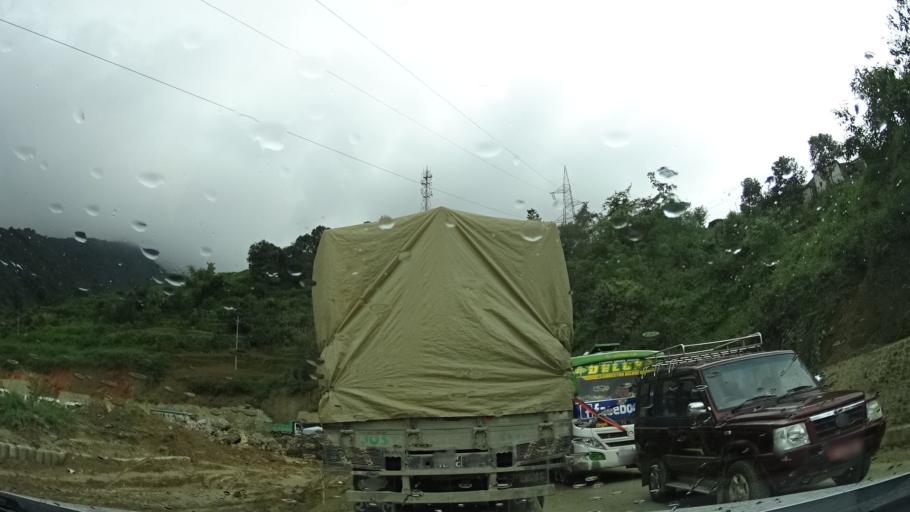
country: NP
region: Central Region
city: Kirtipur
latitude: 27.7047
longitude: 85.2060
